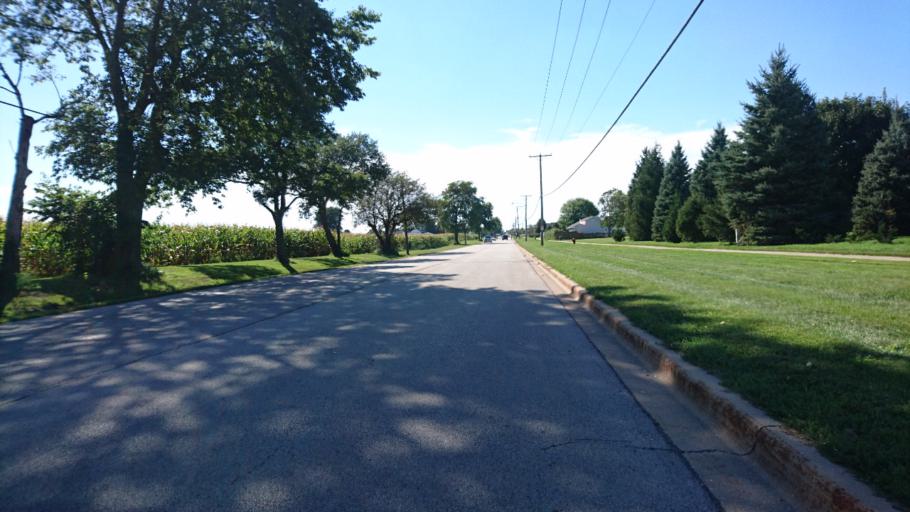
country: US
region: Illinois
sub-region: Will County
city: New Lenox
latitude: 41.5117
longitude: -87.9974
